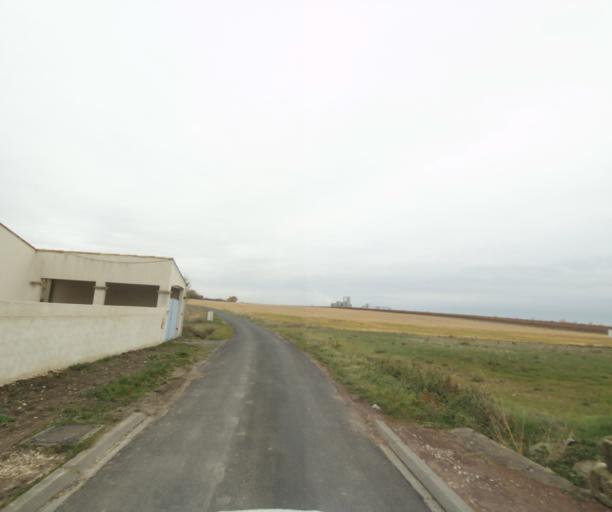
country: FR
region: Poitou-Charentes
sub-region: Departement de la Charente-Maritime
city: Chermignac
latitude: 45.7110
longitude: -0.6641
